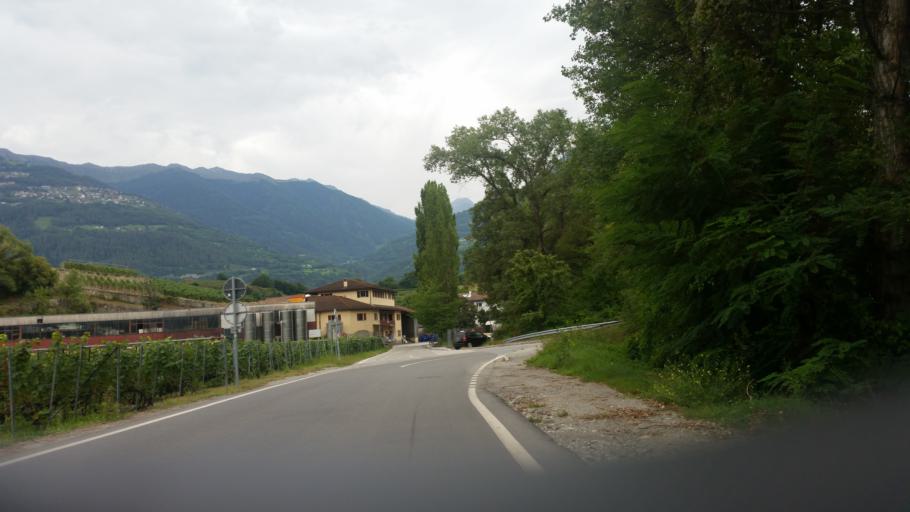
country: CH
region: Valais
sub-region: Conthey District
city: Conthey
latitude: 46.2267
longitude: 7.3134
